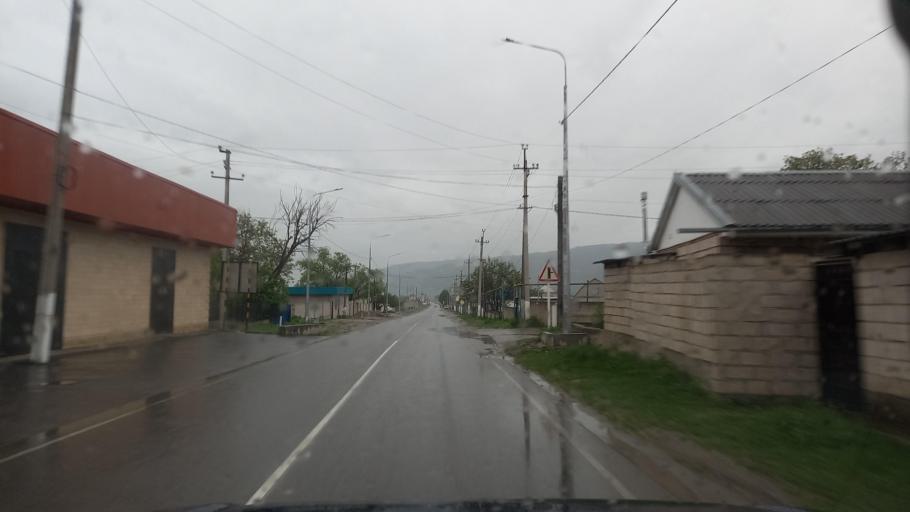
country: RU
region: Kabardino-Balkariya
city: Gundelen
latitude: 43.5897
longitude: 43.1983
